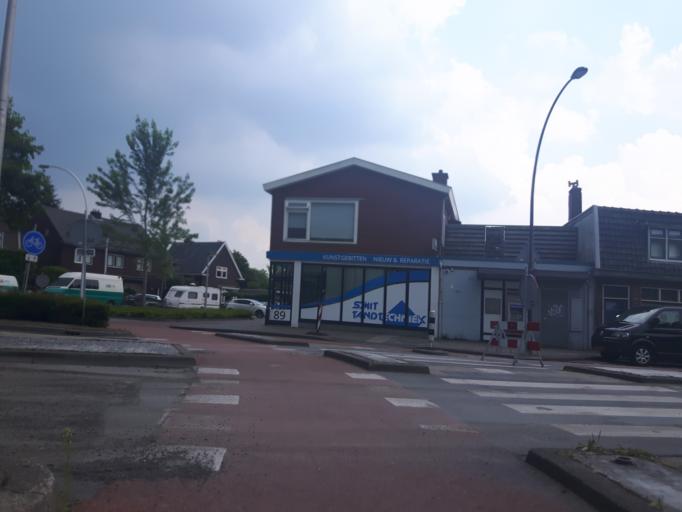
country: NL
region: Overijssel
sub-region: Gemeente Hengelo
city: Hengelo
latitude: 52.2735
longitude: 6.8022
